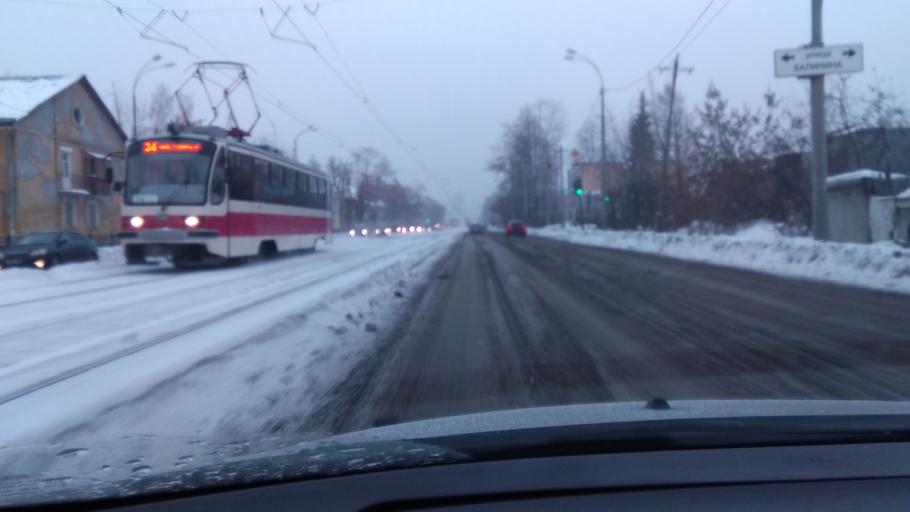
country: RU
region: Sverdlovsk
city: Yekaterinburg
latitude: 56.9005
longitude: 60.5815
